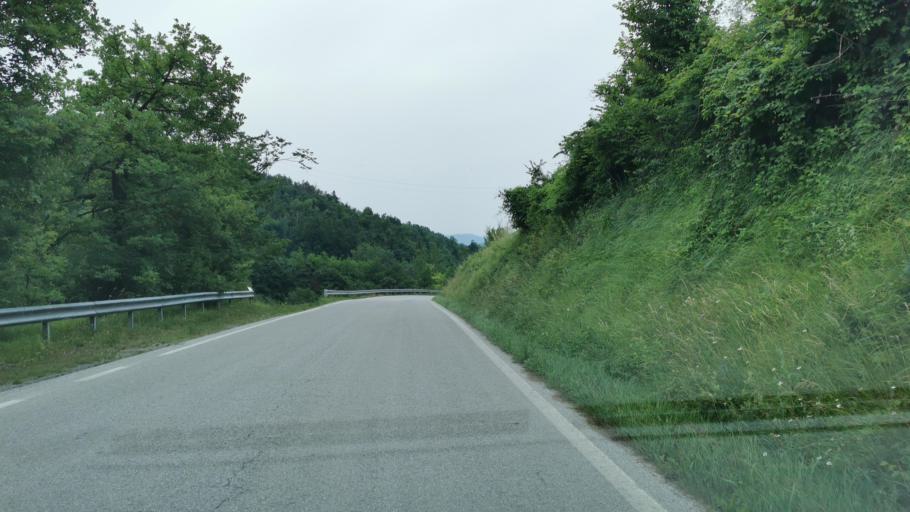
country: IT
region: Piedmont
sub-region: Provincia di Cuneo
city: Torresina
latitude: 44.4109
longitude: 8.0479
